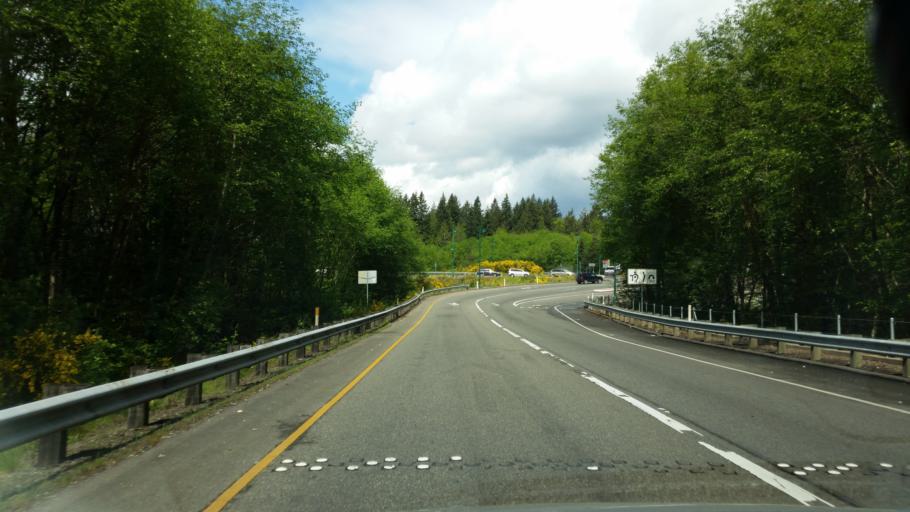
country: US
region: Washington
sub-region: Pierce County
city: Canterwood
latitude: 47.3570
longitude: -122.6132
